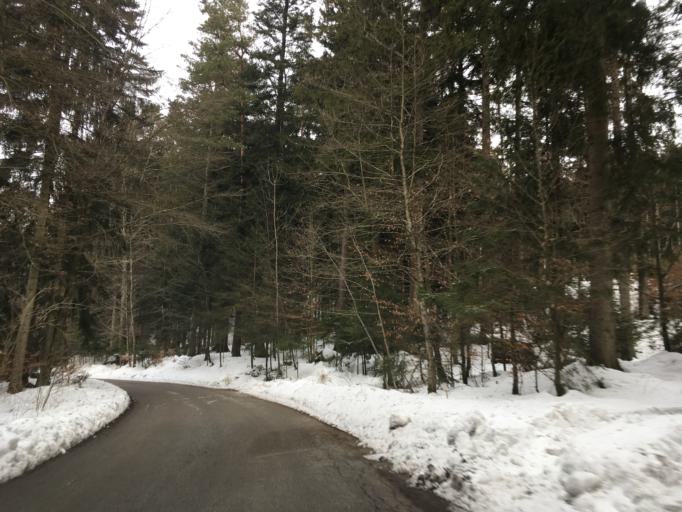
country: DE
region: Bavaria
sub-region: Upper Bavaria
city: Schnaitsee
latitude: 48.0419
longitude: 12.3618
